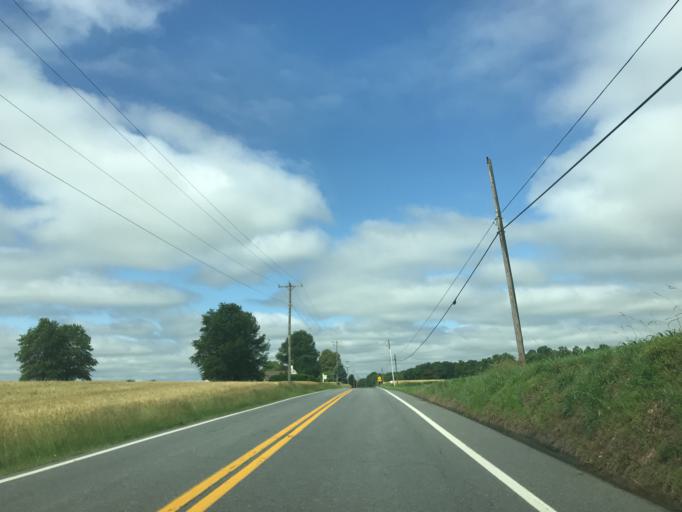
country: US
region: Maryland
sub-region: Caroline County
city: Ridgely
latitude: 38.8854
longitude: -75.9703
